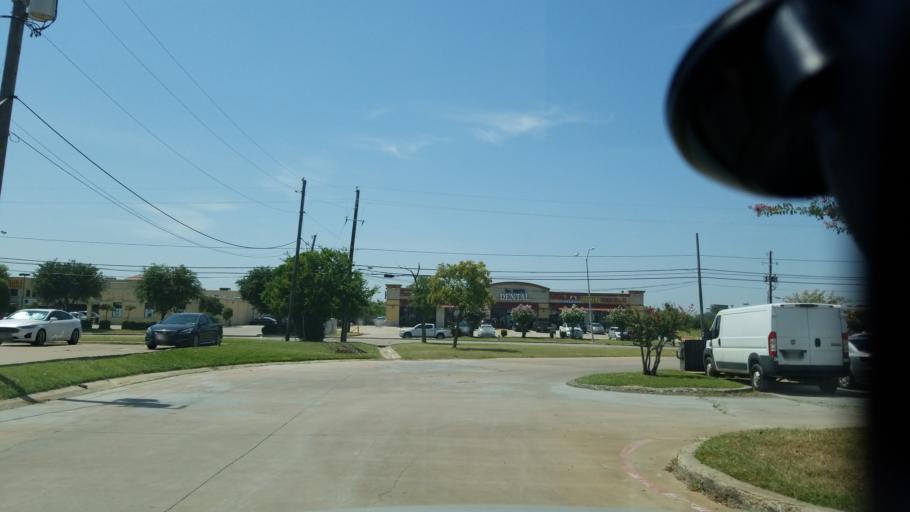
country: US
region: Texas
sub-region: Dallas County
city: Farmers Branch
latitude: 32.8962
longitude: -96.9039
